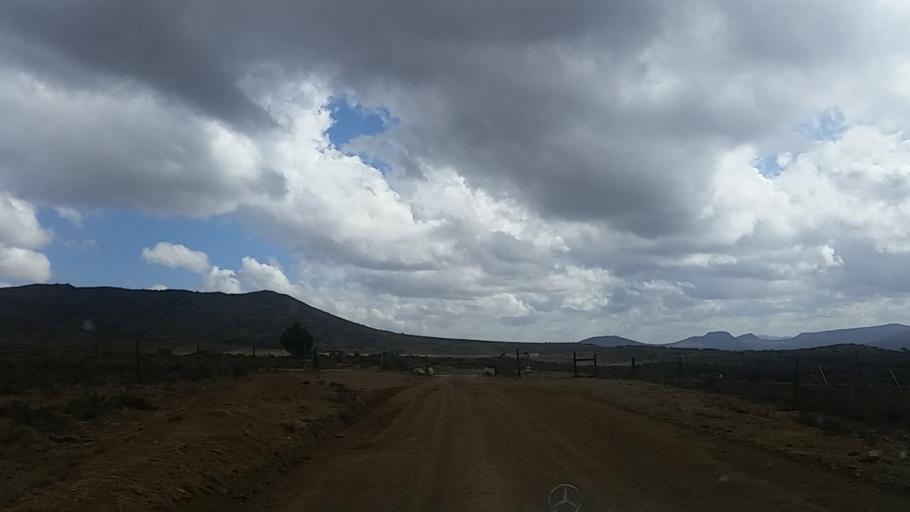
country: ZA
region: Eastern Cape
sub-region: Chris Hani District Municipality
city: Middelburg
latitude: -31.7910
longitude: 24.6631
